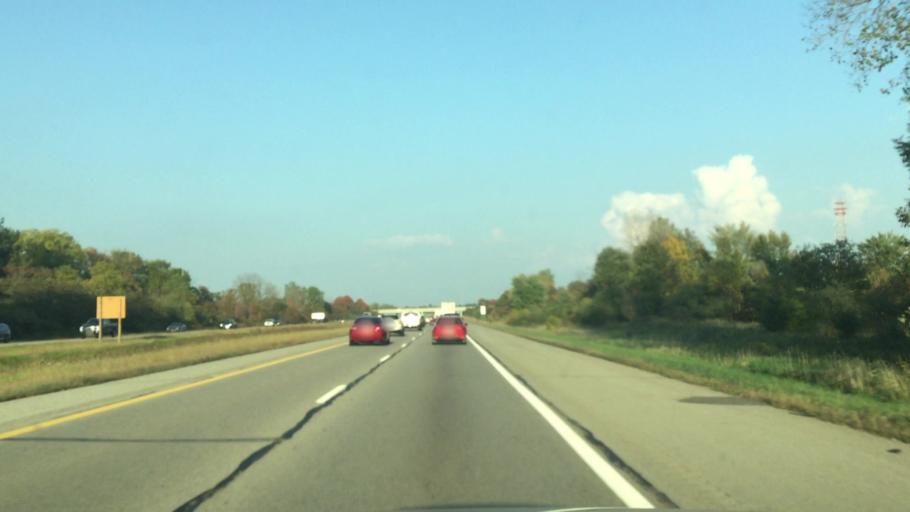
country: US
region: Michigan
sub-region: Wayne County
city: Plymouth
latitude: 42.3646
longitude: -83.5576
